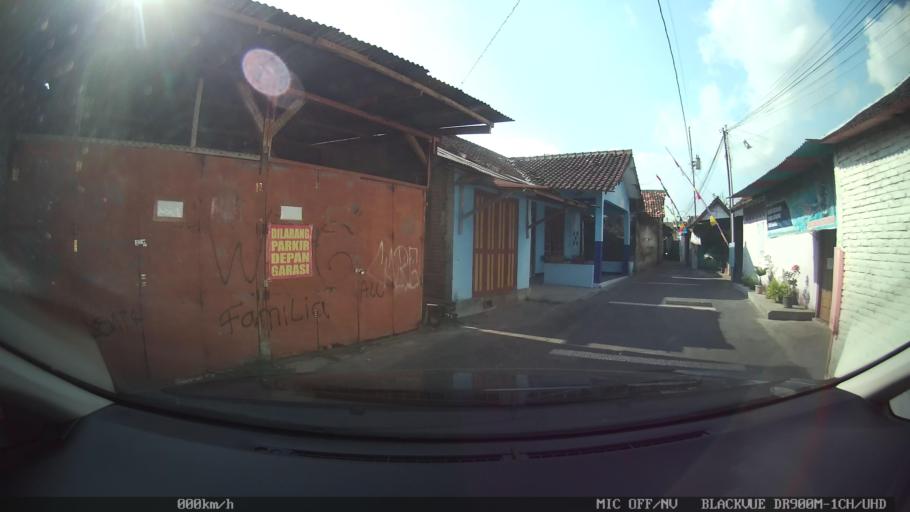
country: ID
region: Daerah Istimewa Yogyakarta
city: Sewon
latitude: -7.8317
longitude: 110.3958
